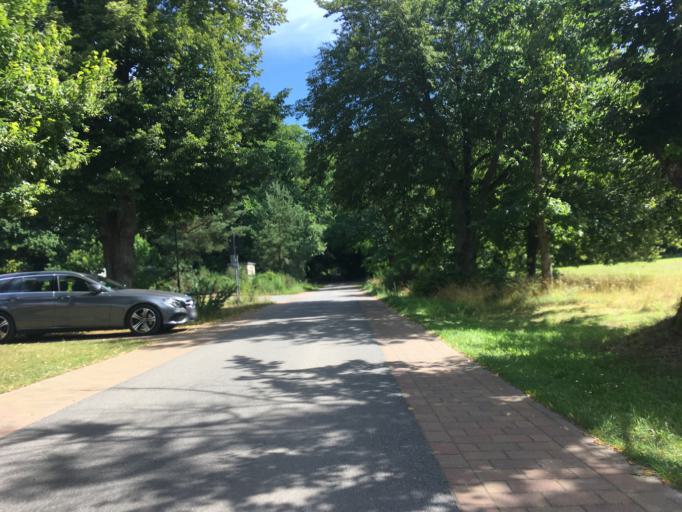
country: DE
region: Brandenburg
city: Rheinsberg
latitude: 53.0889
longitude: 12.8964
